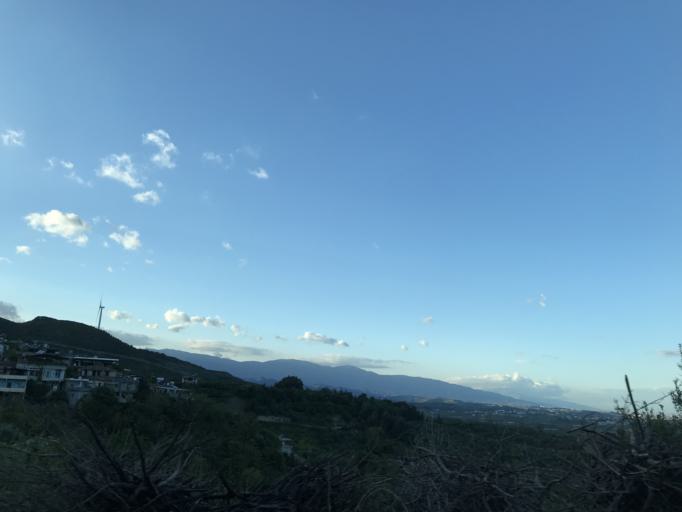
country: TR
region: Hatay
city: Buyukcat
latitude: 36.1001
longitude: 36.0557
